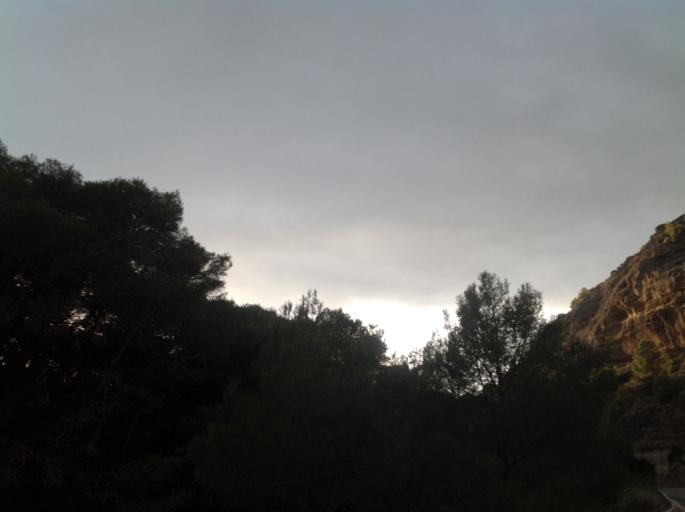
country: ES
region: Andalusia
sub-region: Provincia de Malaga
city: Carratraca
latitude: 36.9124
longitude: -4.7821
